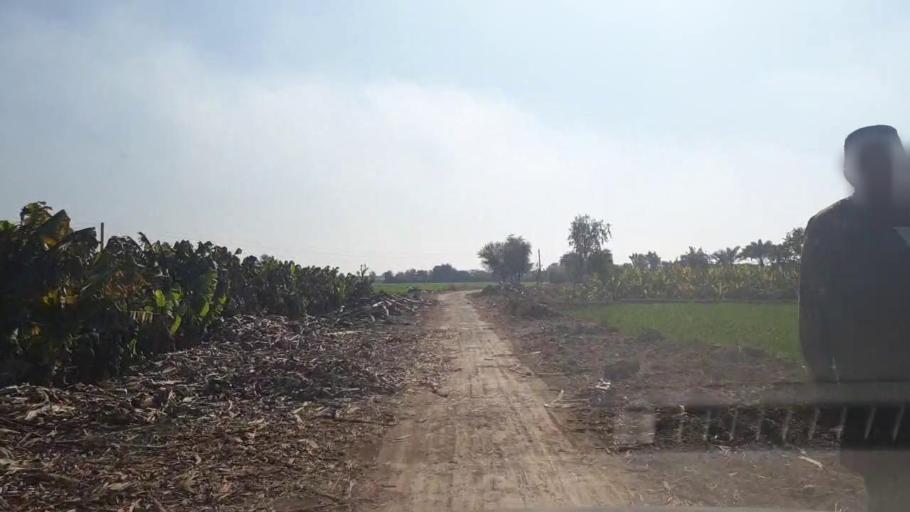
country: PK
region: Sindh
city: Shahdadpur
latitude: 25.9166
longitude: 68.5725
